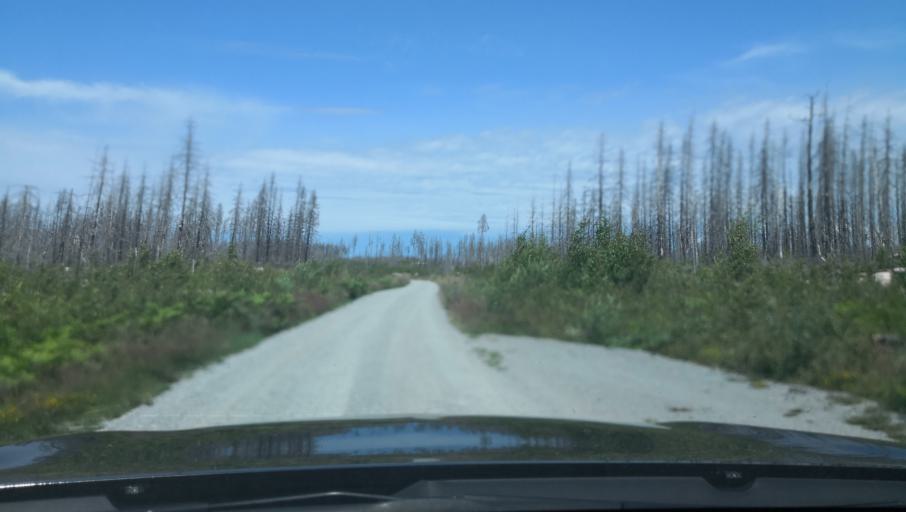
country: SE
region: Vaestmanland
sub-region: Surahammars Kommun
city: Ramnas
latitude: 59.9075
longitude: 16.1473
